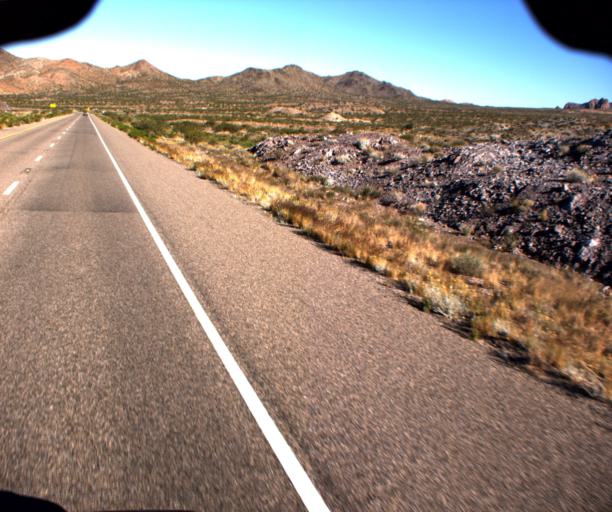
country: US
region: Nevada
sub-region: Clark County
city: Laughlin
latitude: 35.1978
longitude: -114.4170
